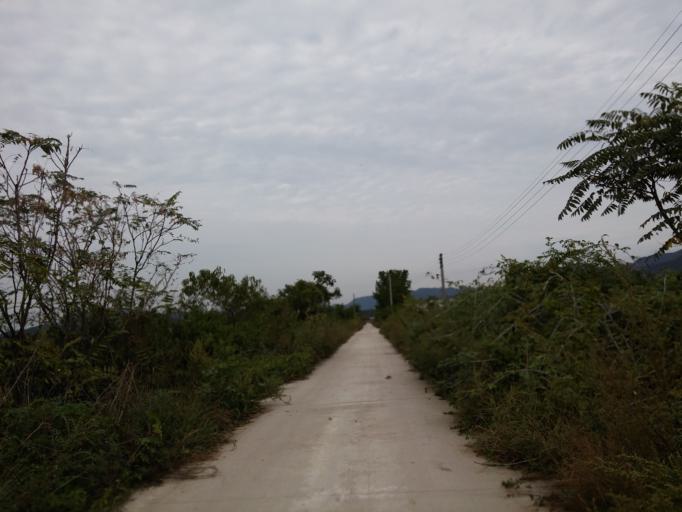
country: KR
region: Chungcheongnam-do
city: Yonmu
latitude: 36.1660
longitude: 127.2011
